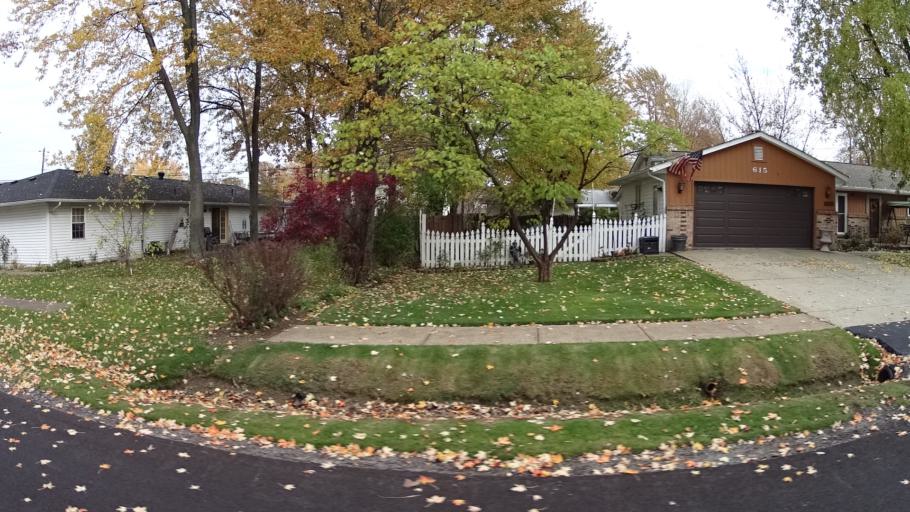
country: US
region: Ohio
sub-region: Lorain County
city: Sheffield Lake
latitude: 41.4901
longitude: -82.1030
